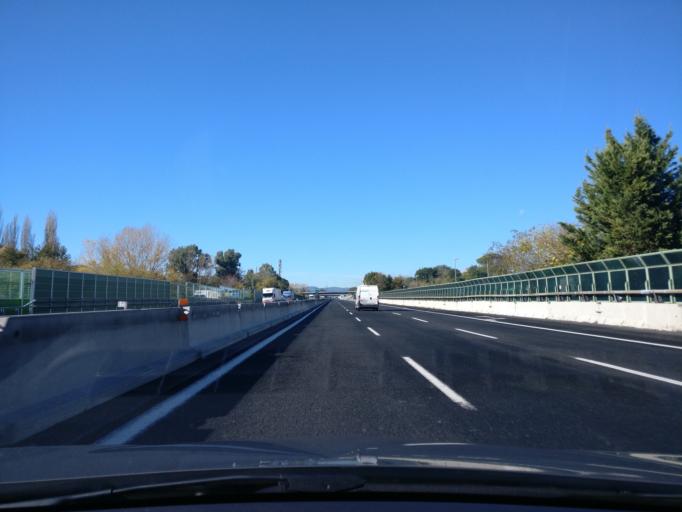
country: IT
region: Latium
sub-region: Provincia di Frosinone
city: Ceprano
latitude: 41.5430
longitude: 13.5144
